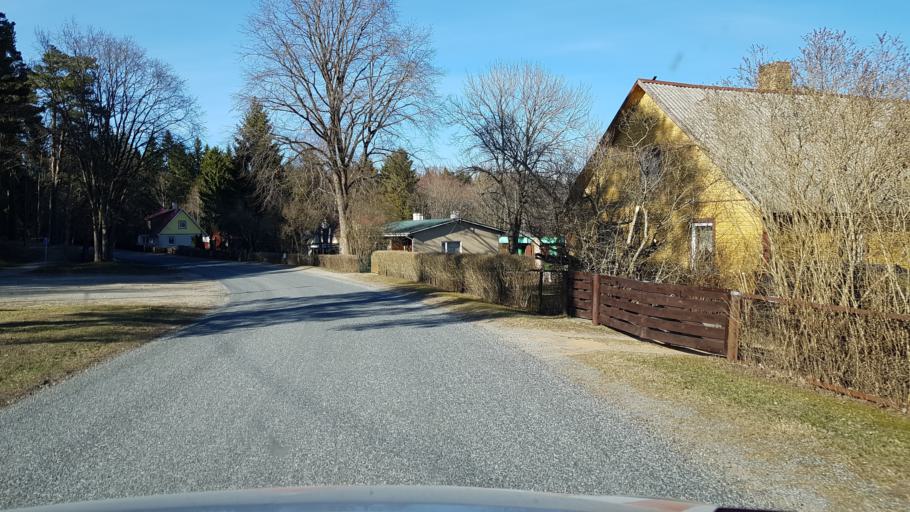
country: EE
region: Laeaene-Virumaa
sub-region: Vinni vald
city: Vinni
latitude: 59.1666
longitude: 26.5917
